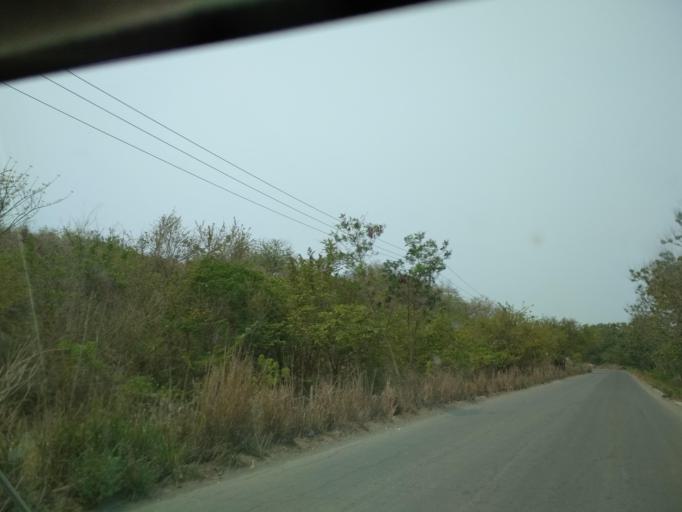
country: MX
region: Veracruz
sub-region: Veracruz
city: Delfino Victoria (Santa Fe)
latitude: 19.1834
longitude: -96.3210
